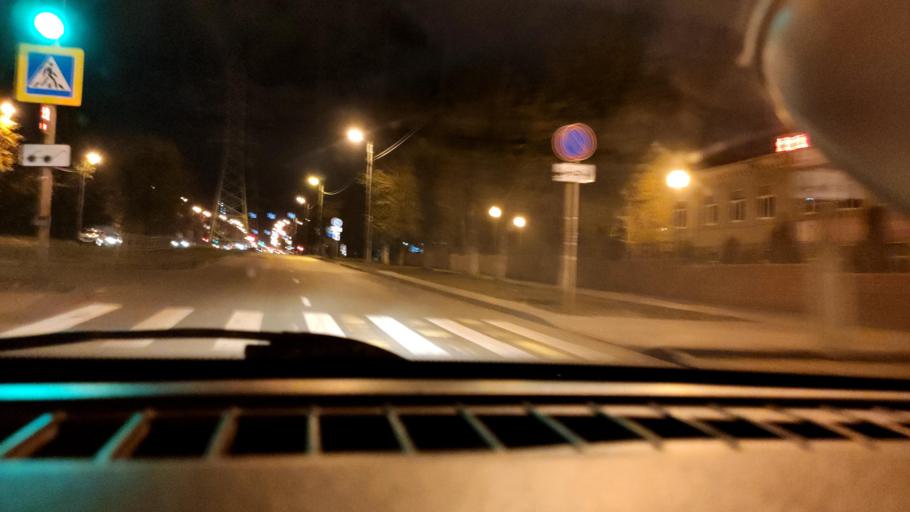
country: RU
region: Samara
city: Samara
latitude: 53.1993
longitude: 50.2143
